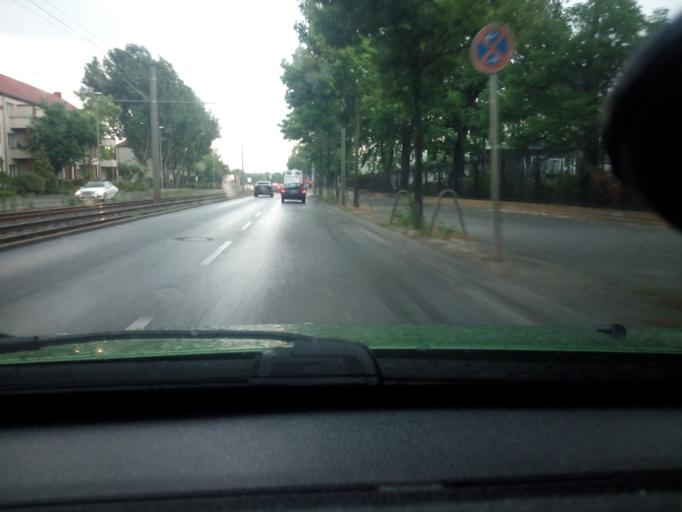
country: DE
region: Berlin
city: Rummelsburg
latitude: 52.4980
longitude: 13.4830
